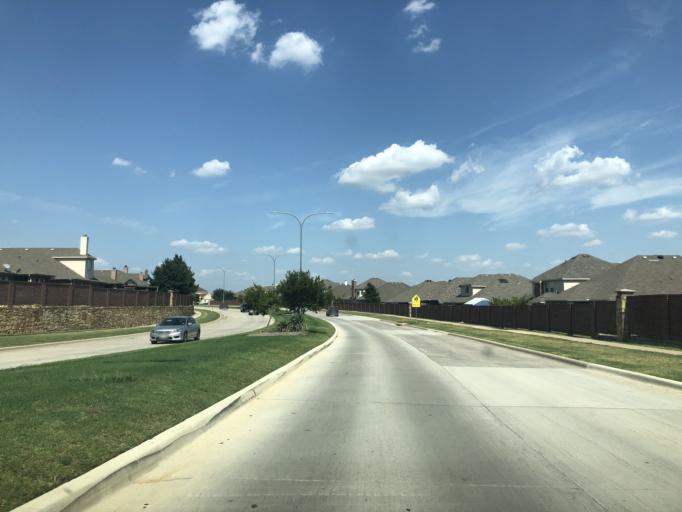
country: US
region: Texas
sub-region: Tarrant County
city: Haslet
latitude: 32.9240
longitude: -97.3308
